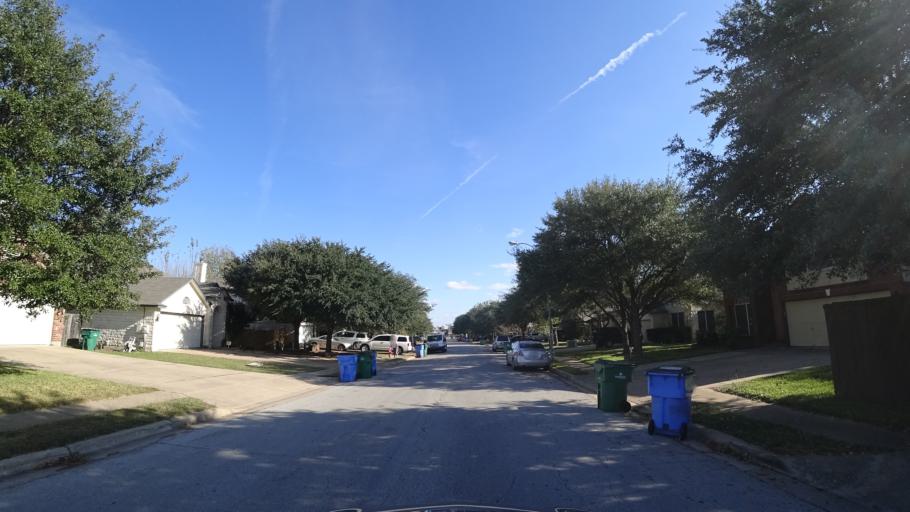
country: US
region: Texas
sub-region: Travis County
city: Wells Branch
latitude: 30.4587
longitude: -97.6847
